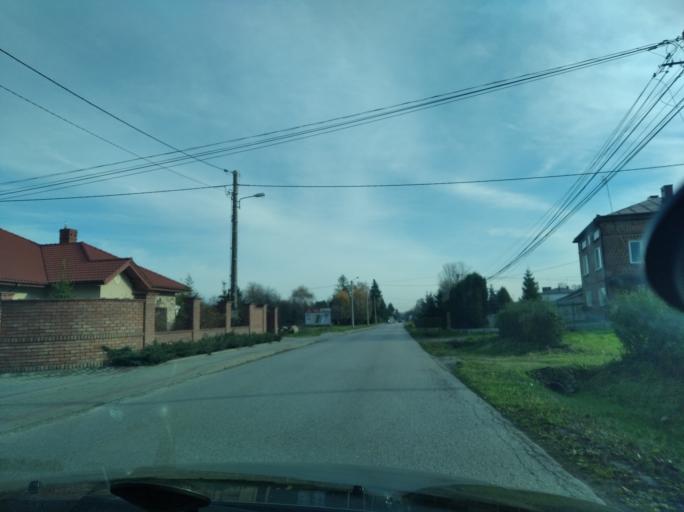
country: PL
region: Subcarpathian Voivodeship
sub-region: Powiat lancucki
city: Kraczkowa
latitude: 50.0379
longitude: 22.1529
